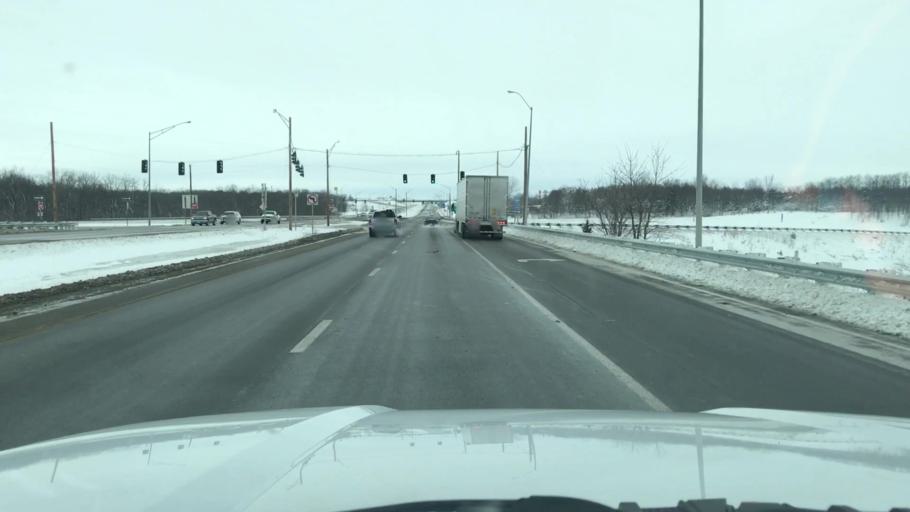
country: US
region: Missouri
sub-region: Clinton County
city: Cameron
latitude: 39.7538
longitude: -94.2173
